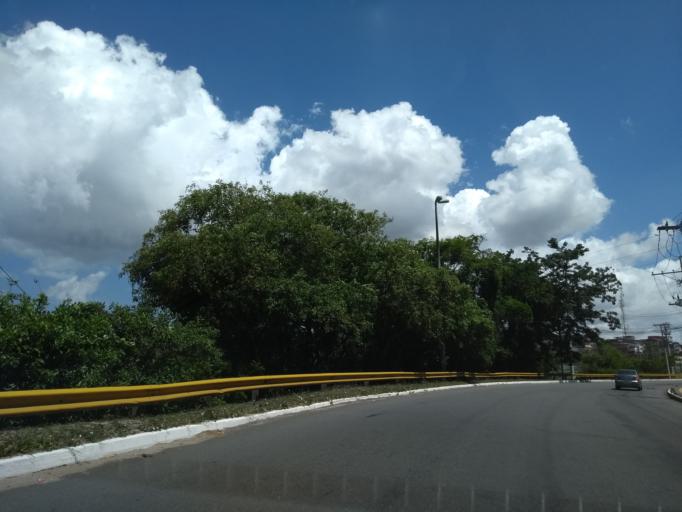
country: BR
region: Bahia
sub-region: Salvador
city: Salvador
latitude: -12.9769
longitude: -38.4539
